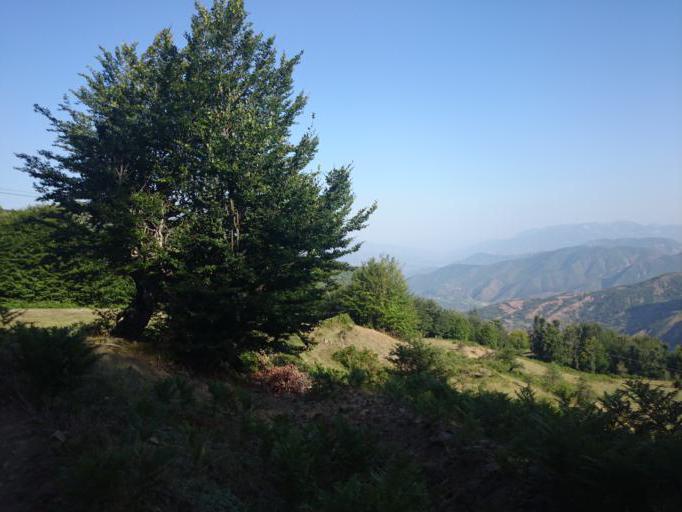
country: AL
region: Elbasan
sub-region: Rrethi i Librazhdit
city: Orenje
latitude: 41.3040
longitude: 20.1516
